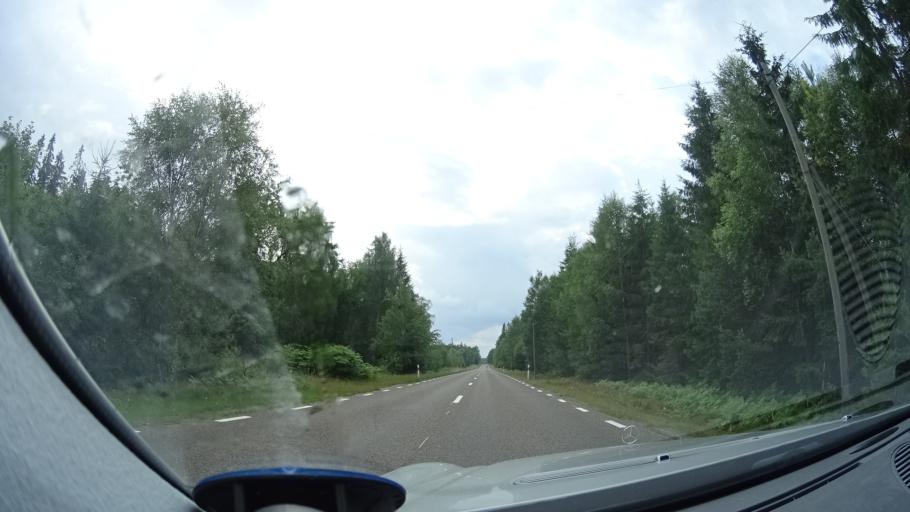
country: SE
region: Kalmar
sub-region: Emmaboda Kommun
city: Emmaboda
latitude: 56.6494
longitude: 15.6882
